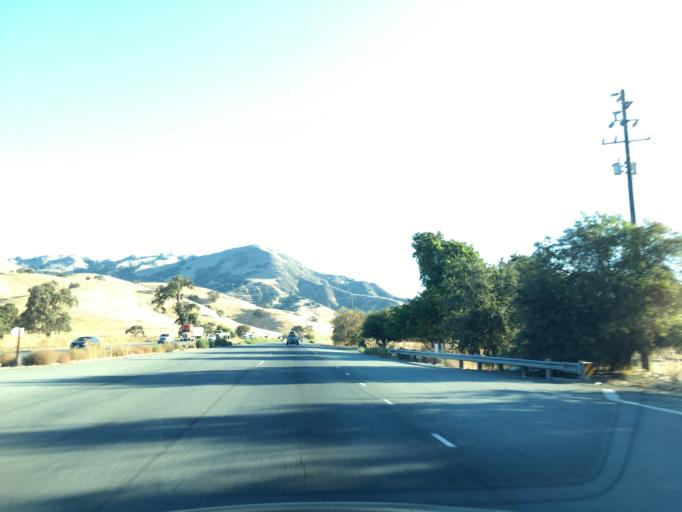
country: US
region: California
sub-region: San Benito County
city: Hollister
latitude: 37.0023
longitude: -121.3712
